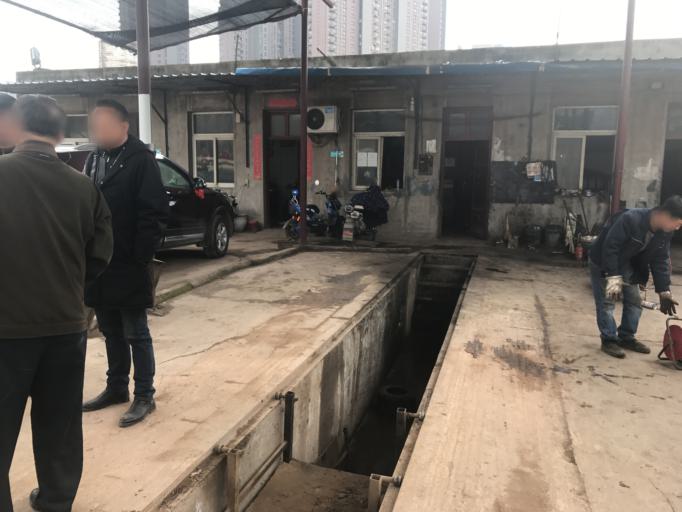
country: CN
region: Hubei
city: Heping
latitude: 30.6084
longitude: 114.3689
